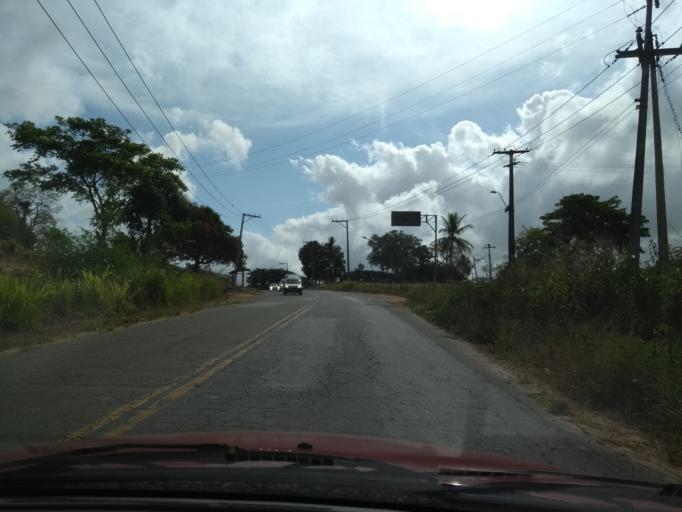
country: BR
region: Bahia
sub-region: Sao Francisco Do Conde
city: Sao Francisco do Conde
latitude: -12.6097
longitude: -38.6460
